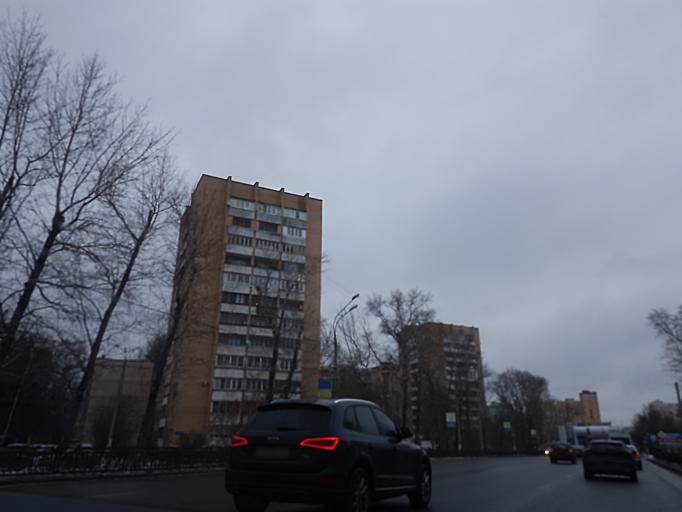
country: RU
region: Moskovskaya
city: Pavshino
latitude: 55.8110
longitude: 37.3406
